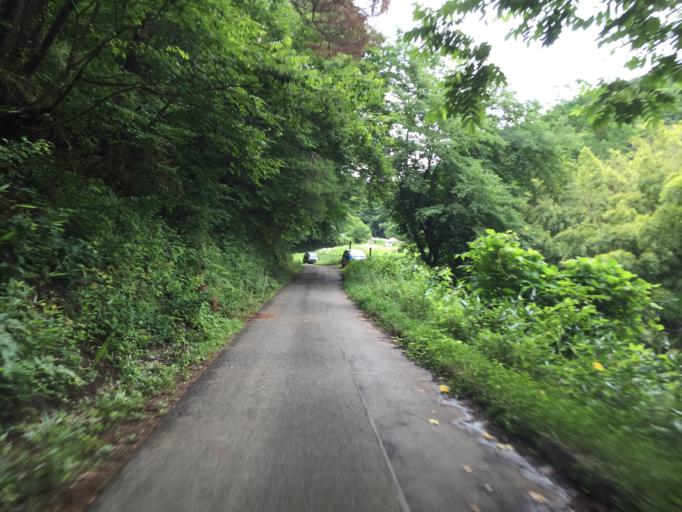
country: JP
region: Fukushima
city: Fukushima-shi
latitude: 37.7341
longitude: 140.4891
